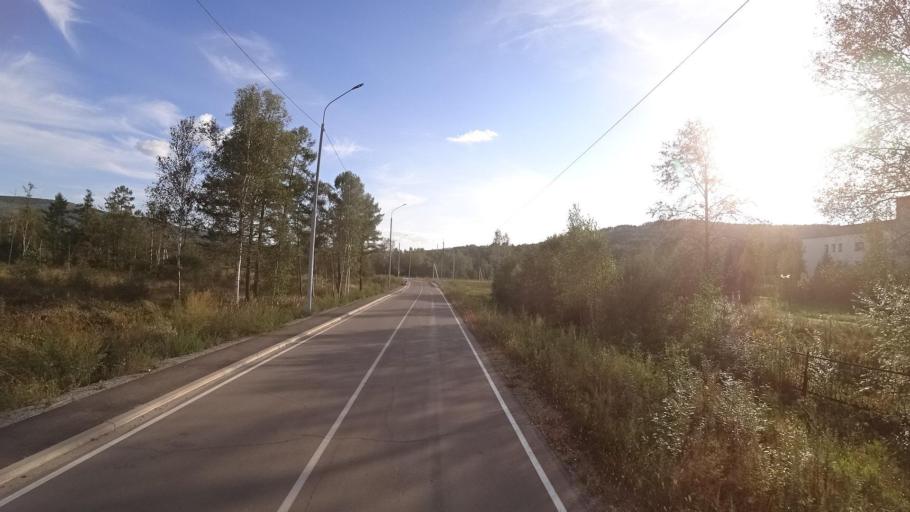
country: RU
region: Jewish Autonomous Oblast
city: Kul'dur
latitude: 49.2127
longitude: 131.6247
